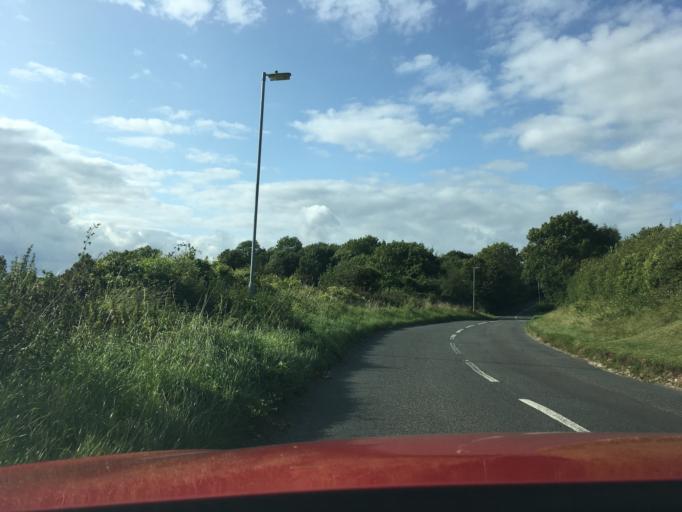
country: GB
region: England
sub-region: South Gloucestershire
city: Falfield
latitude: 51.6191
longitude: -2.4384
